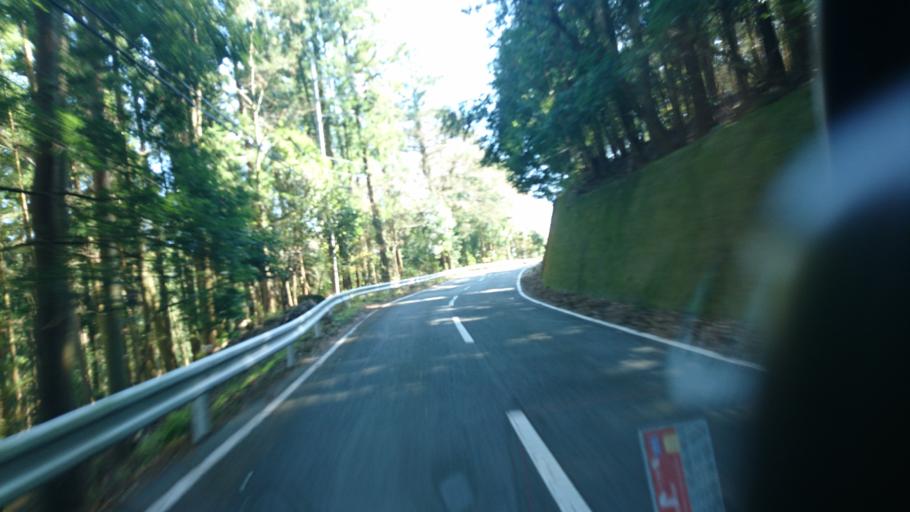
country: JP
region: Shizuoka
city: Fujinomiya
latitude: 35.3455
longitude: 138.4384
